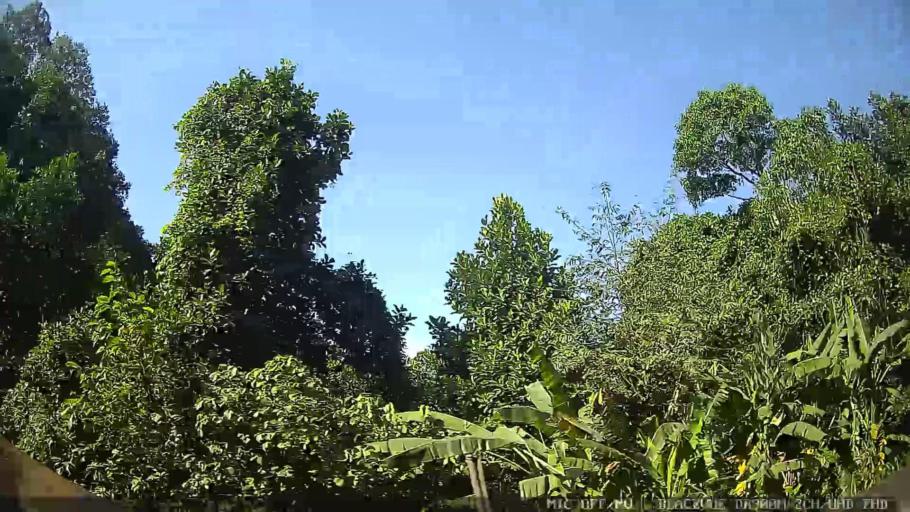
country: BR
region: Sao Paulo
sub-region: Cubatao
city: Cubatao
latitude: -23.8888
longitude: -46.4637
